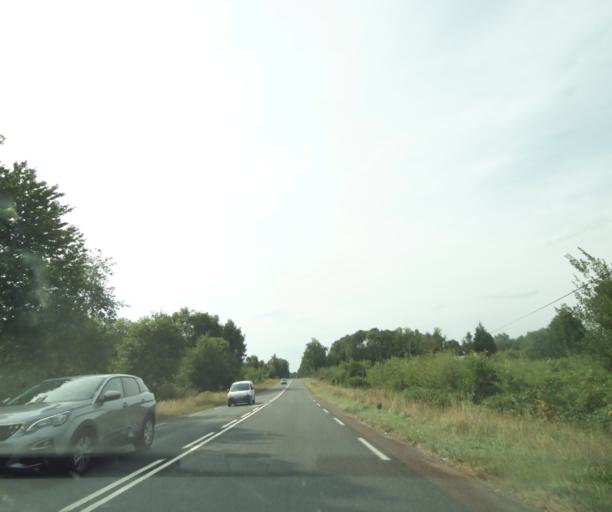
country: FR
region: Pays de la Loire
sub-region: Departement de la Sarthe
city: Marigne-Laille
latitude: 47.7975
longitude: 0.3311
